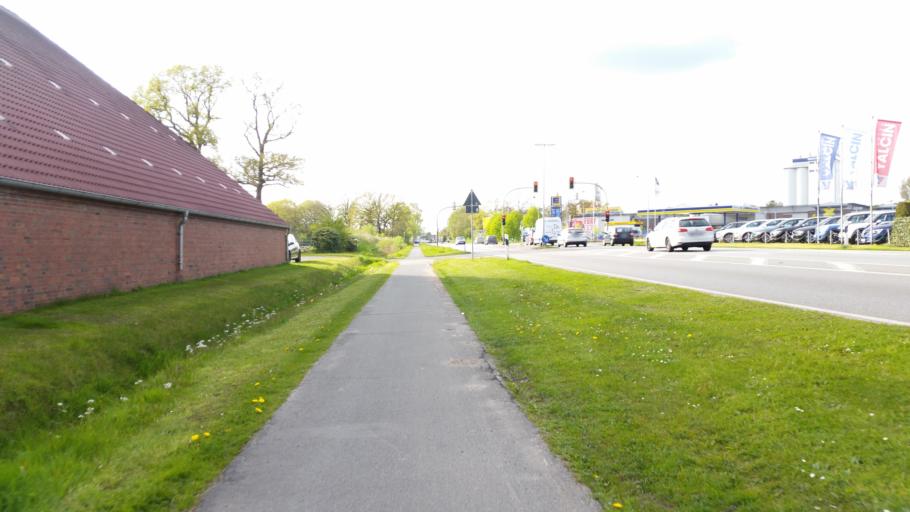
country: DE
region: Lower Saxony
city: Aurich
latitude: 53.4563
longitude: 7.4981
